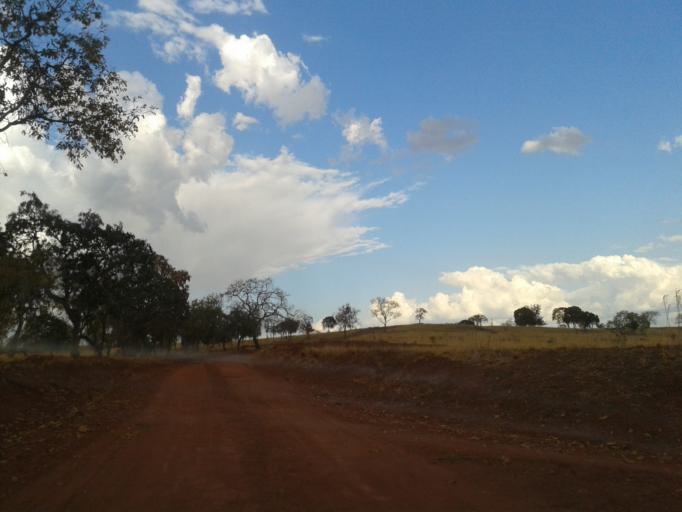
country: BR
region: Minas Gerais
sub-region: Santa Vitoria
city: Santa Vitoria
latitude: -19.1820
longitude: -49.9447
